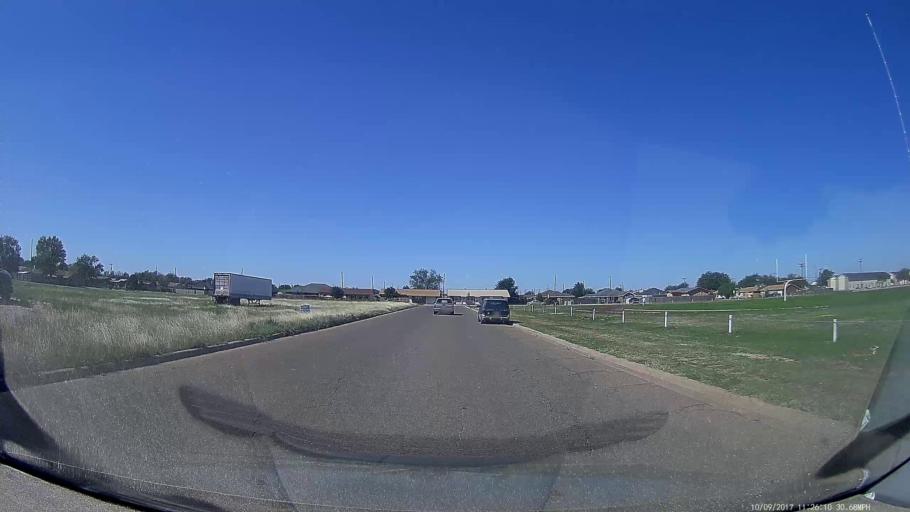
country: US
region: New Mexico
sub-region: Curry County
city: Clovis
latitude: 34.4111
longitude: -103.2265
